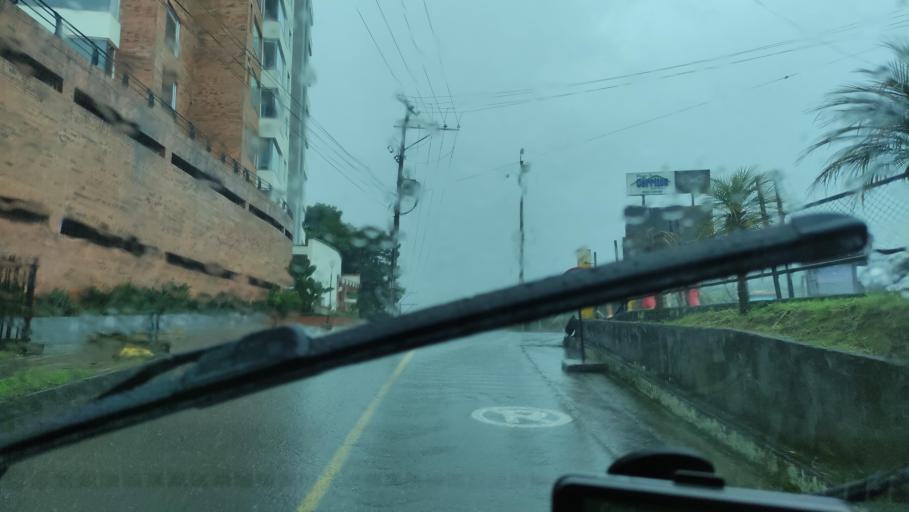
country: CO
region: Caldas
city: Villamaria
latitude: 5.0539
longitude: -75.4754
